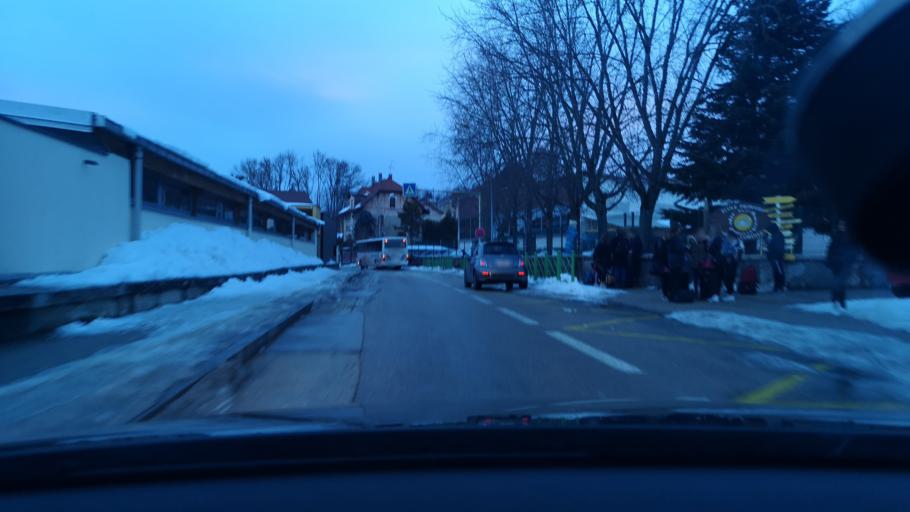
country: FR
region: Franche-Comte
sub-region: Departement du Doubs
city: Pontarlier
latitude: 46.9030
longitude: 6.3602
